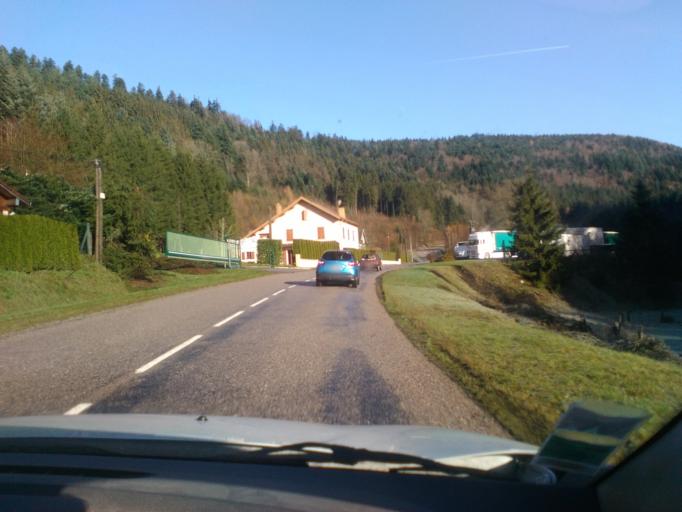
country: FR
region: Lorraine
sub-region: Departement des Vosges
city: Plombieres-les-Bains
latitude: 47.9633
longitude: 6.5243
